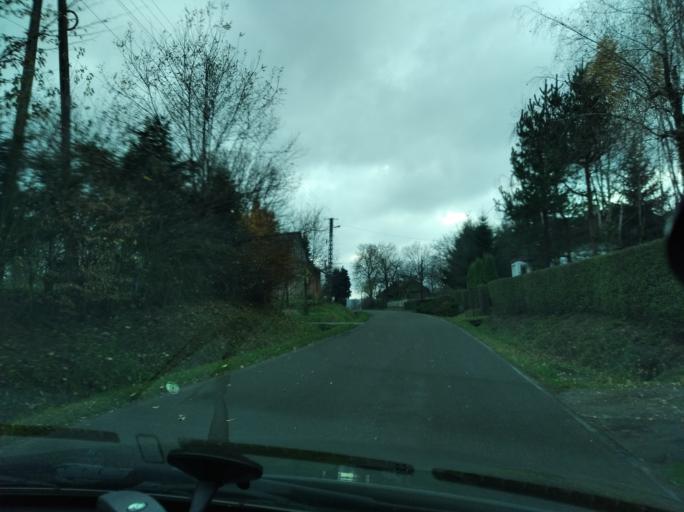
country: PL
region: Subcarpathian Voivodeship
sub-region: Powiat przeworski
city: Sietesz
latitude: 49.9878
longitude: 22.3482
